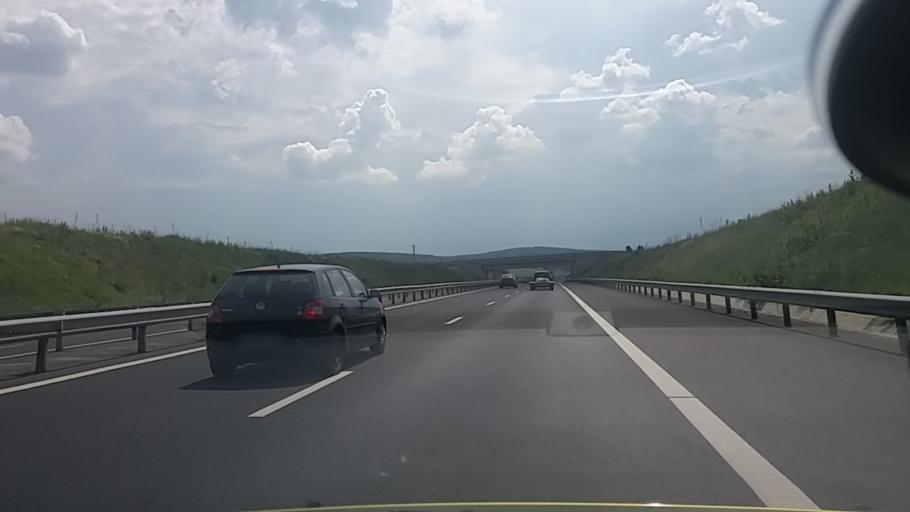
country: RO
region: Hunedoara
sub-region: Comuna Turdas
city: Turdas
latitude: 45.8495
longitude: 23.1339
